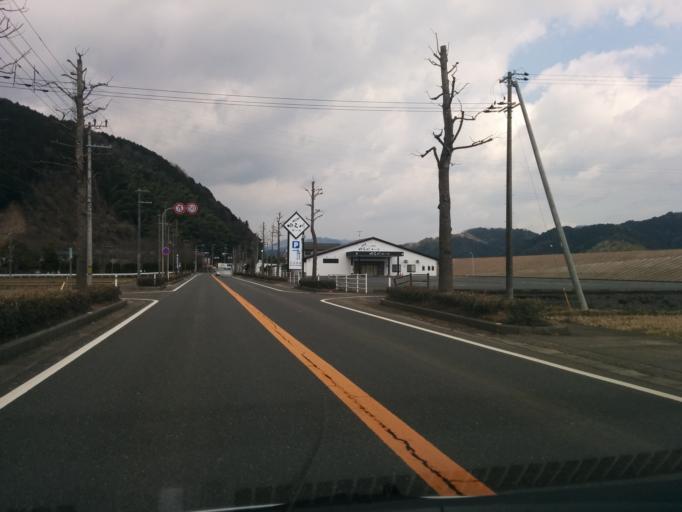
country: JP
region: Kyoto
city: Maizuru
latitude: 35.4370
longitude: 135.2548
